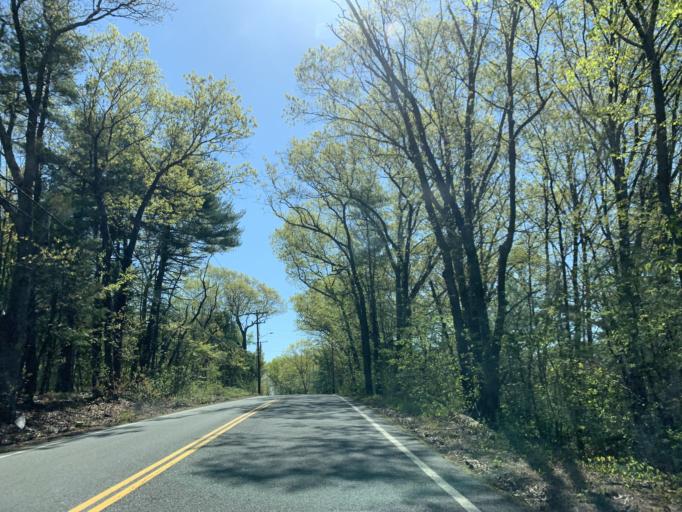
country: US
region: Massachusetts
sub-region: Middlesex County
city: West Concord
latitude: 42.4178
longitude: -71.3932
